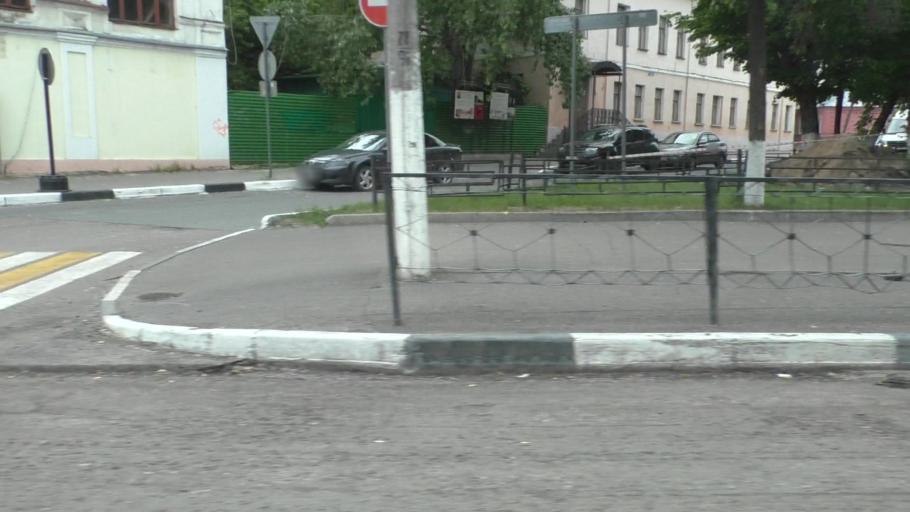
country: RU
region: Moskovskaya
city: Yegor'yevsk
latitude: 55.3851
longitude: 39.0323
